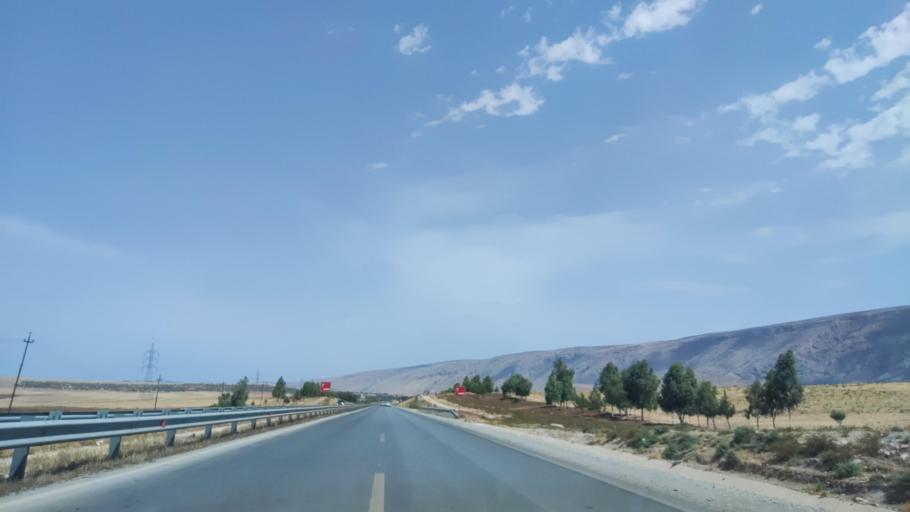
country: IQ
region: Arbil
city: Shaqlawah
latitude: 36.4628
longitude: 44.3835
